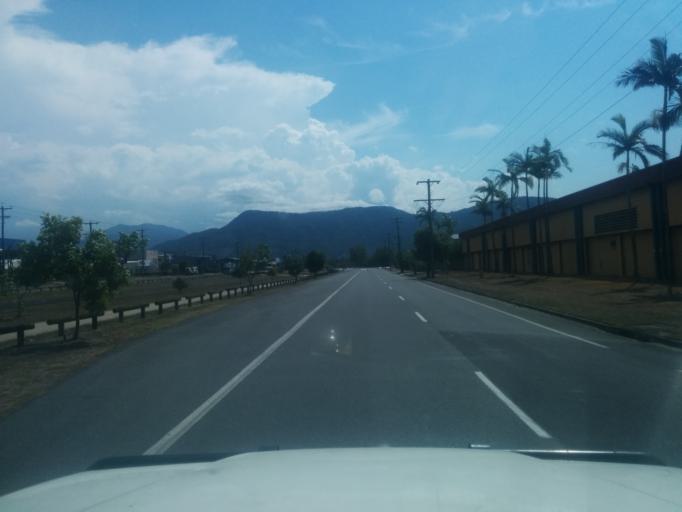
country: AU
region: Queensland
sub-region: Cairns
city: Woree
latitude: -16.9385
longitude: 145.7583
